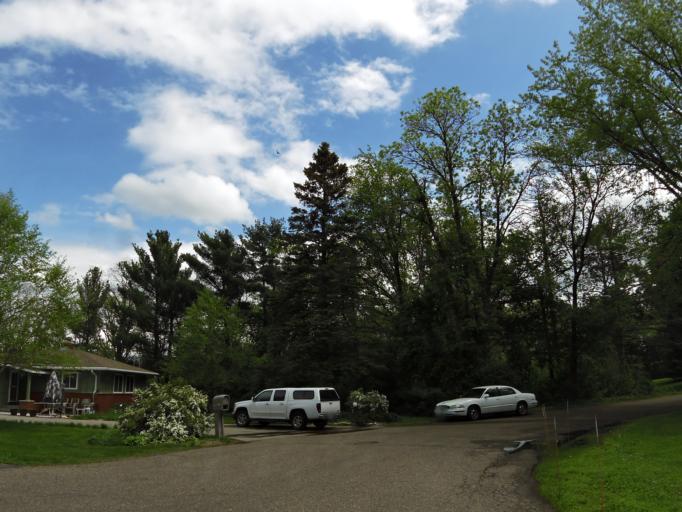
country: US
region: Wisconsin
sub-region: Saint Croix County
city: Hudson
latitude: 44.9822
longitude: -92.7409
